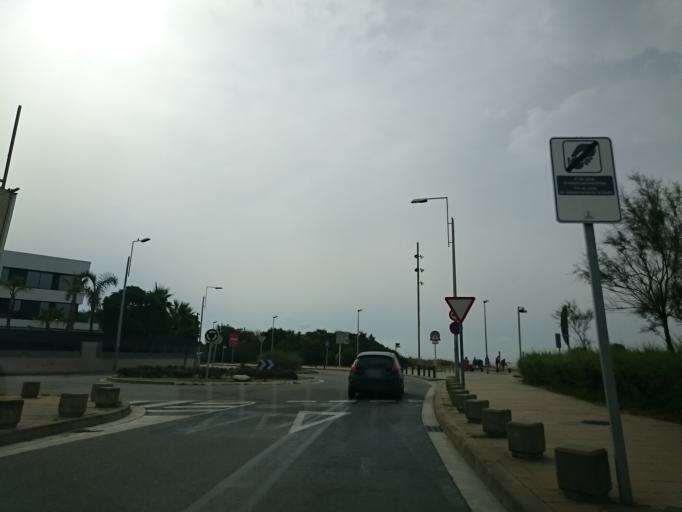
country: ES
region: Catalonia
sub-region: Provincia de Barcelona
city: Castelldefels
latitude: 41.2657
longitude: 2.0018
